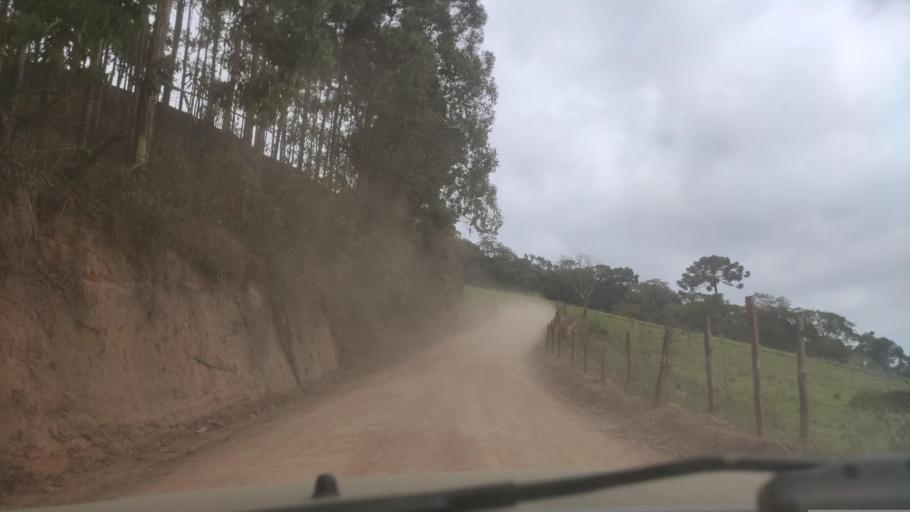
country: BR
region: Minas Gerais
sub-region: Paraisopolis
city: Paraisopolis
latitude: -22.6604
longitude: -45.9016
